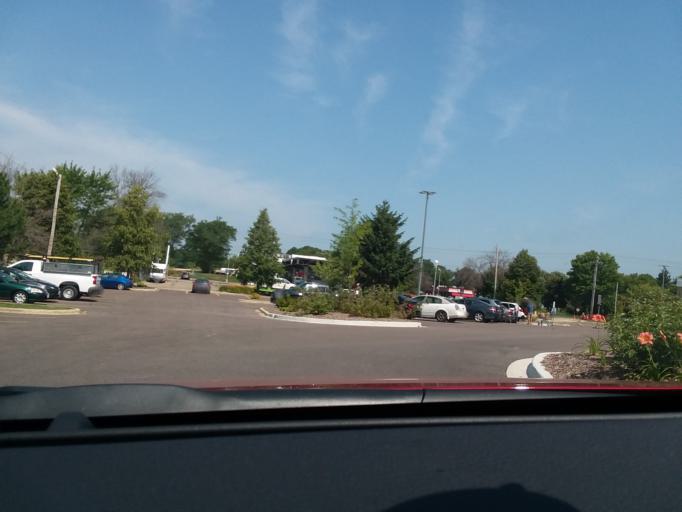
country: US
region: Wisconsin
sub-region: Dane County
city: Monona
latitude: 43.1198
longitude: -89.3170
